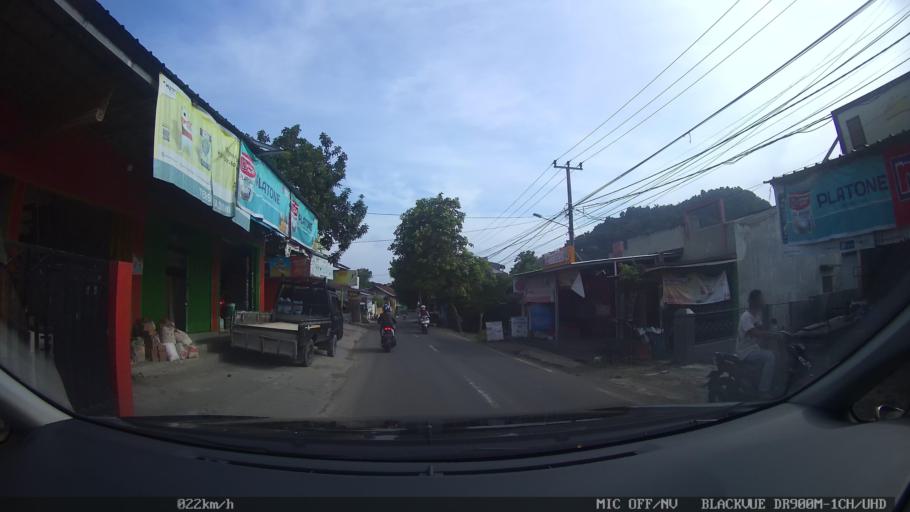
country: ID
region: Lampung
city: Kedaton
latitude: -5.3933
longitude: 105.2662
